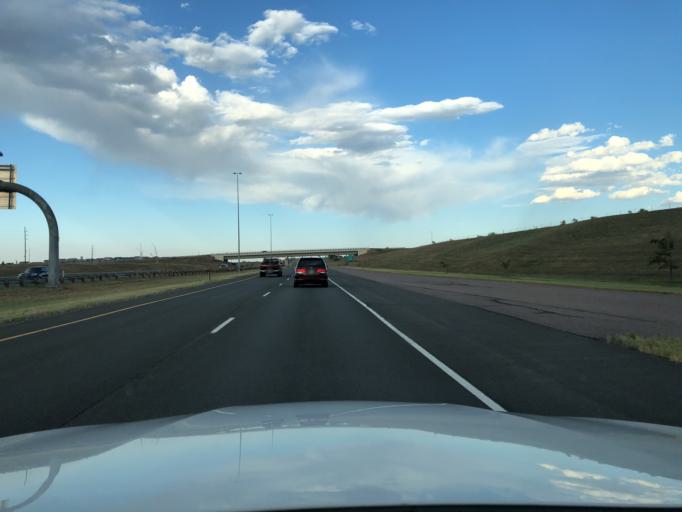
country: US
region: Colorado
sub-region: Boulder County
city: Lafayette
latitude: 39.9804
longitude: -105.0396
